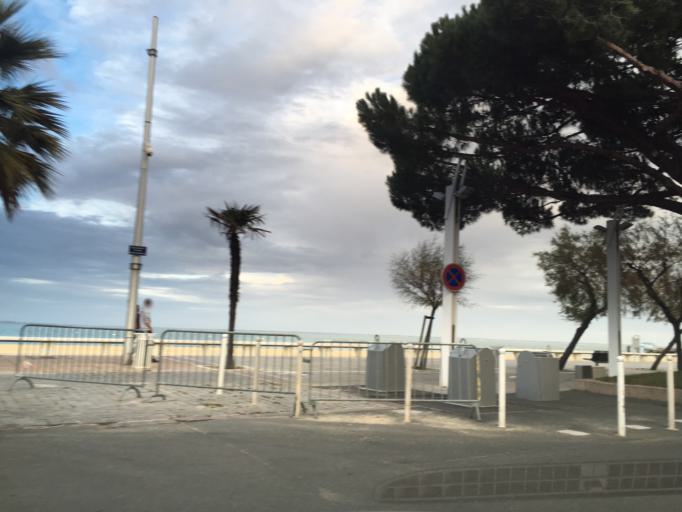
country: FR
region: Aquitaine
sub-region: Departement de la Gironde
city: Arcachon
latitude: 44.6632
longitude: -1.1670
